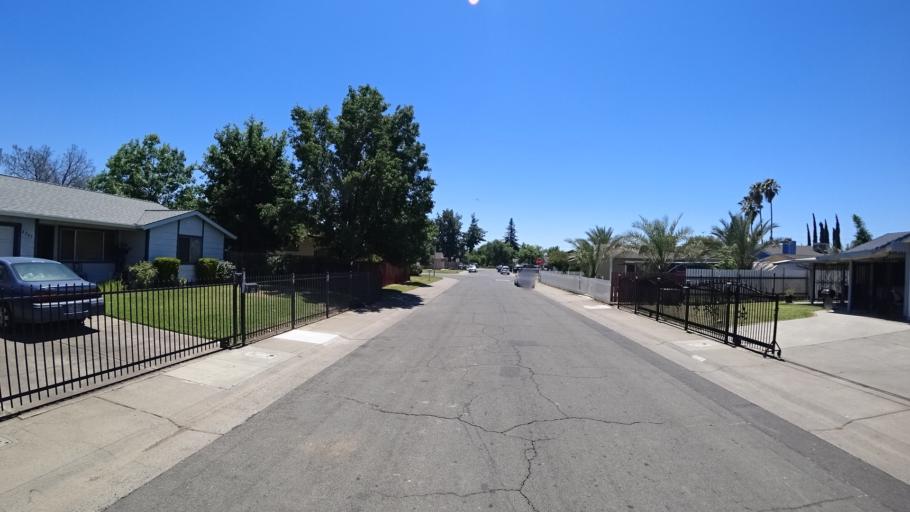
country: US
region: California
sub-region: Sacramento County
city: Parkway
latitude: 38.5356
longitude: -121.4808
